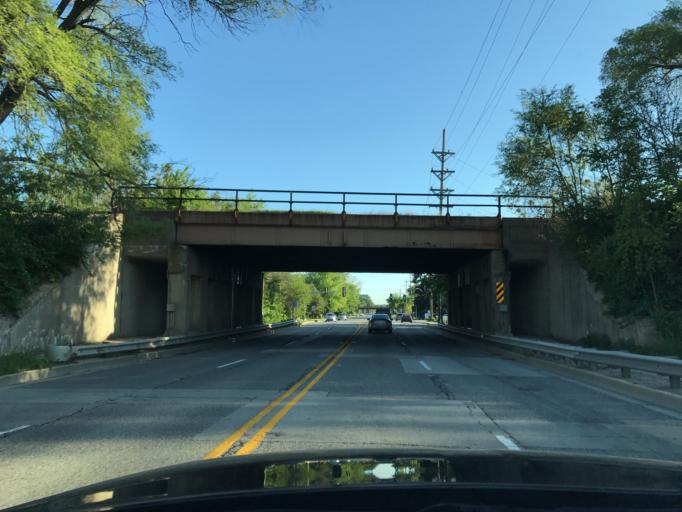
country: US
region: Illinois
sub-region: DuPage County
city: Lisle
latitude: 41.7966
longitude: -88.0772
